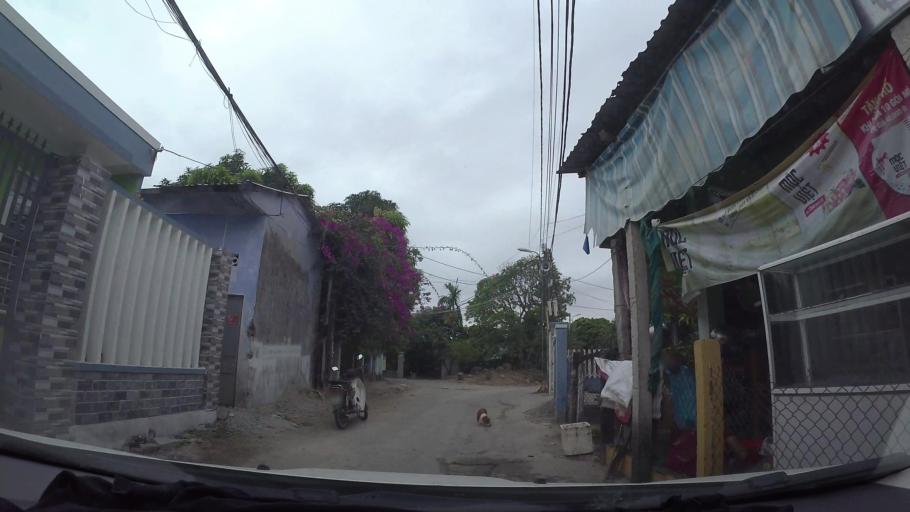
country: VN
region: Da Nang
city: Lien Chieu
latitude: 16.1211
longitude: 108.1175
